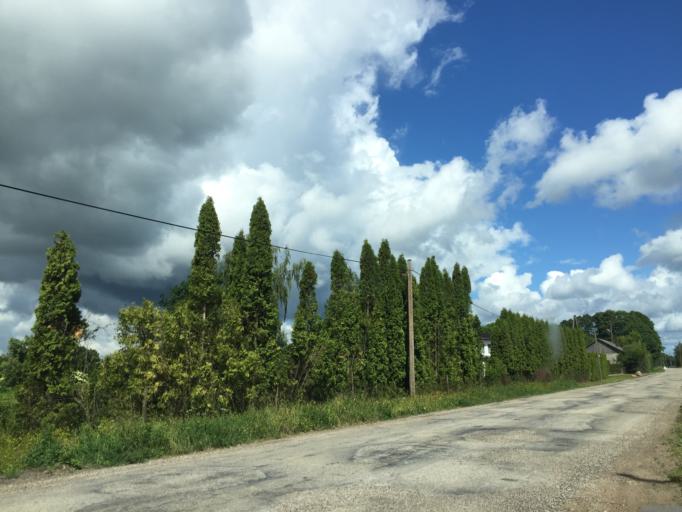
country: LV
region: Lecava
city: Iecava
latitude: 56.6059
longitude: 24.1925
